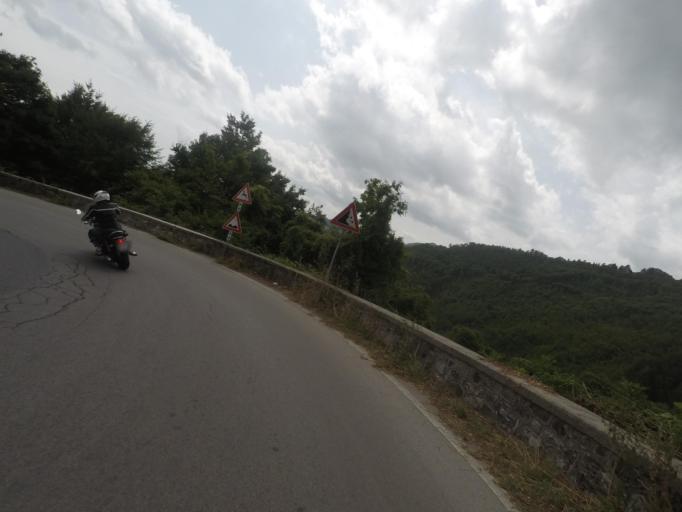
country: IT
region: Tuscany
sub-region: Provincia di Lucca
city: Castelnuovo di Garfagnana
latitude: 44.1060
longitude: 10.3744
